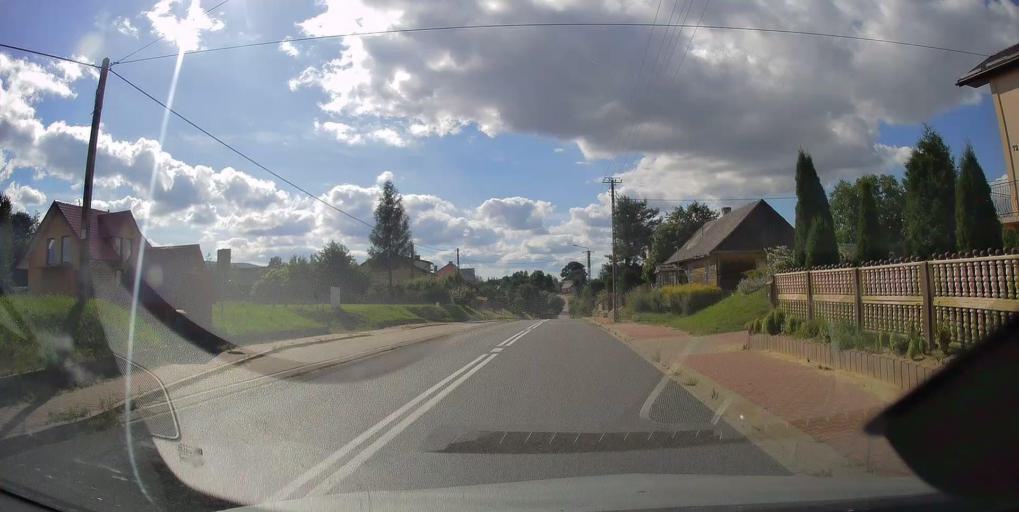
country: PL
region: Swietokrzyskie
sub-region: Powiat kielecki
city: Nowa Slupia
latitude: 50.8834
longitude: 21.0496
